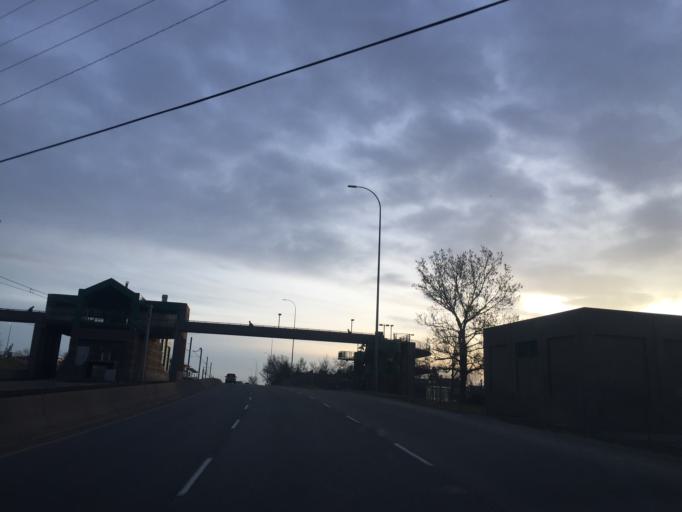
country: CA
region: Alberta
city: Calgary
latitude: 51.0465
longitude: -113.9956
